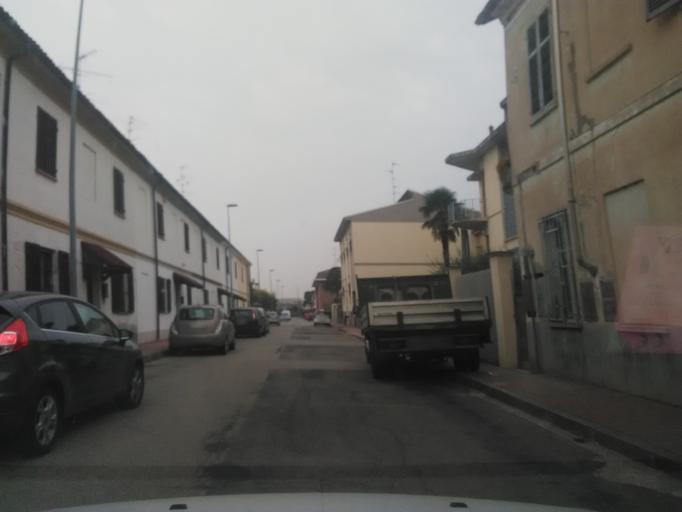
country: IT
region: Piedmont
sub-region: Provincia di Vercelli
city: Vercelli
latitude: 45.3250
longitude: 8.4012
